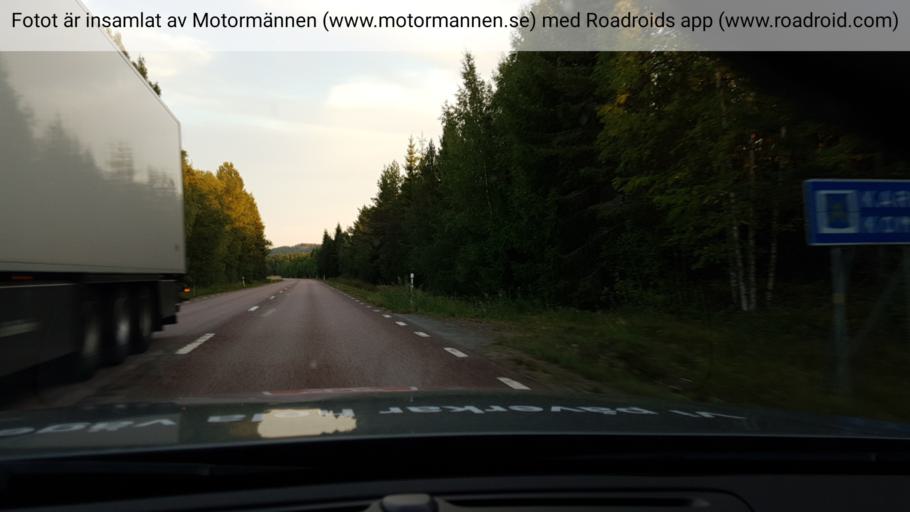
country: SE
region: OErebro
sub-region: Karlskoga Kommun
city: Karlskoga
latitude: 59.4190
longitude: 14.4272
